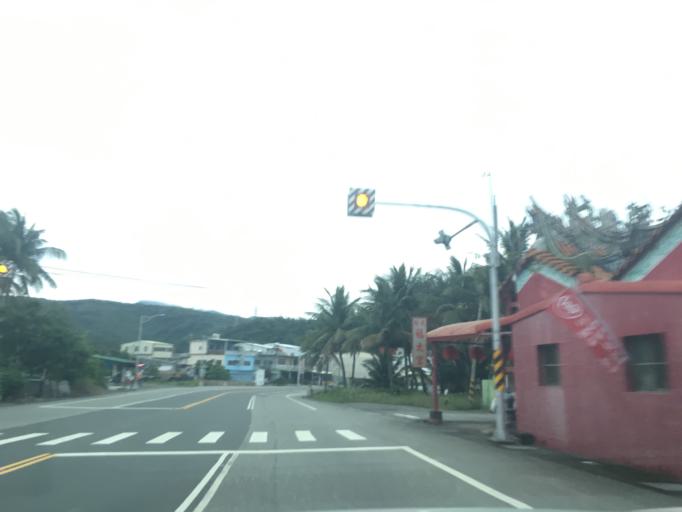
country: TW
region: Taiwan
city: Hengchun
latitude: 22.3377
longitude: 120.8939
